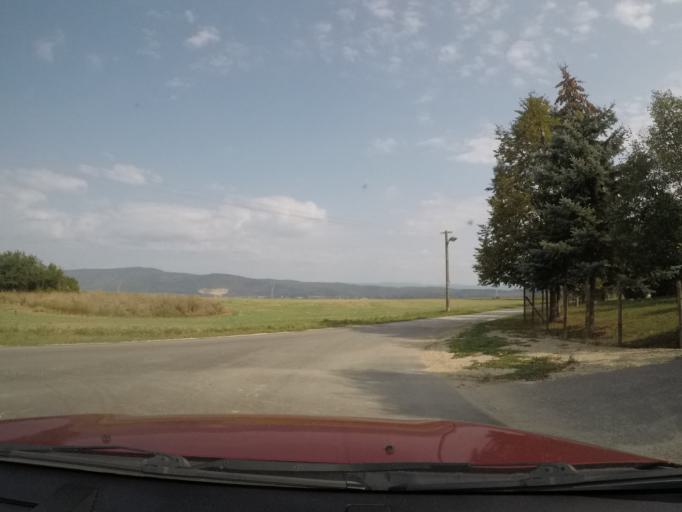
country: SK
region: Kosicky
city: Moldava nad Bodvou
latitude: 48.5812
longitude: 20.9551
